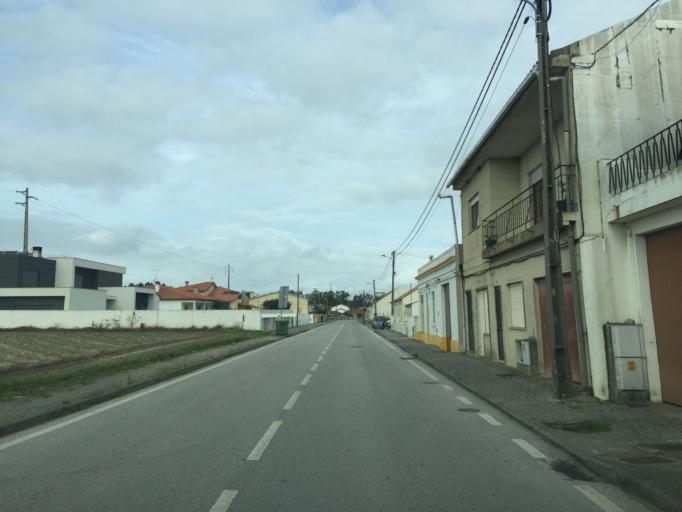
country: PT
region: Coimbra
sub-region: Figueira da Foz
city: Lavos
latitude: 40.0359
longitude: -8.8203
